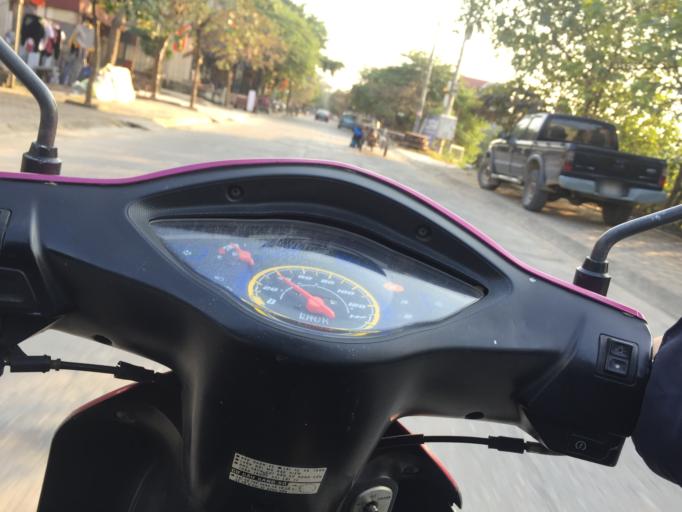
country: VN
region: Ha Noi
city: Chuc Son
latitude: 20.9178
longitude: 105.7142
